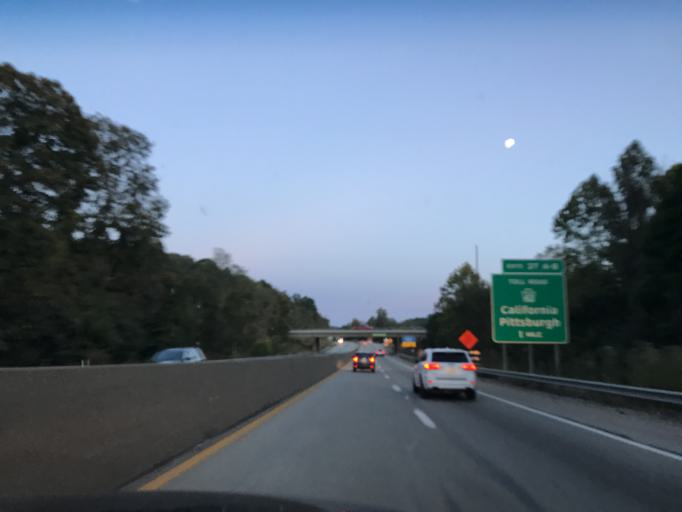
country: US
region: Pennsylvania
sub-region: Washington County
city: Charleroi
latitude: 40.1151
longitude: -79.9430
